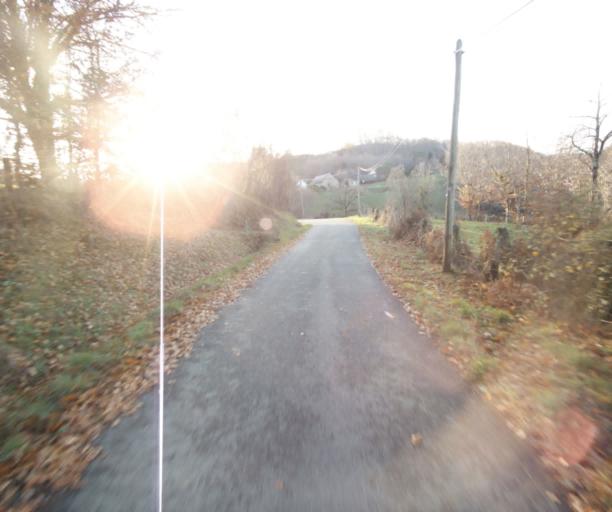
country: FR
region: Limousin
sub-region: Departement de la Correze
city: Laguenne
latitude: 45.2398
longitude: 1.8091
